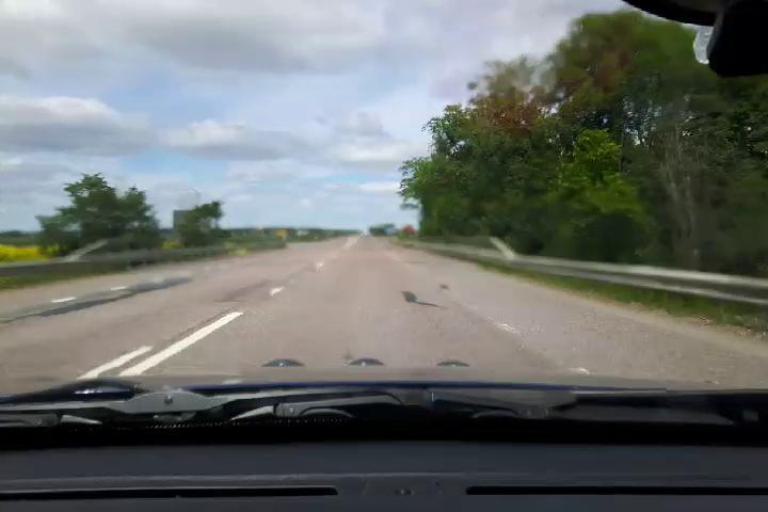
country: SE
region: Uppsala
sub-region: Uppsala Kommun
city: Gamla Uppsala
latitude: 59.9092
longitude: 17.6082
